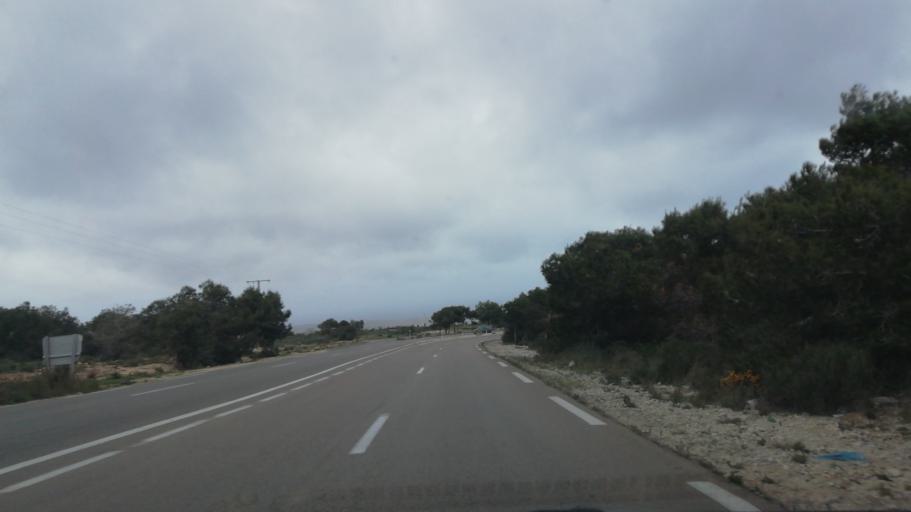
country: DZ
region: Oran
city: Mers el Kebir
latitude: 35.7178
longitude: -0.7408
